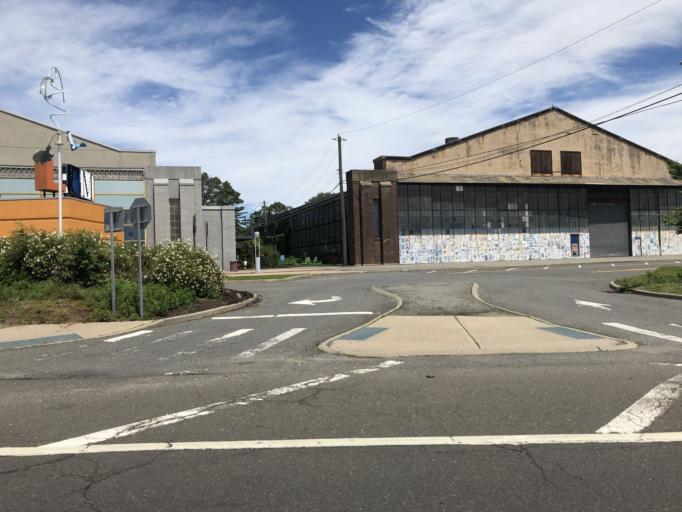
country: US
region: New York
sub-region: Nassau County
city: East Garden City
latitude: 40.7274
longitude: -73.6000
